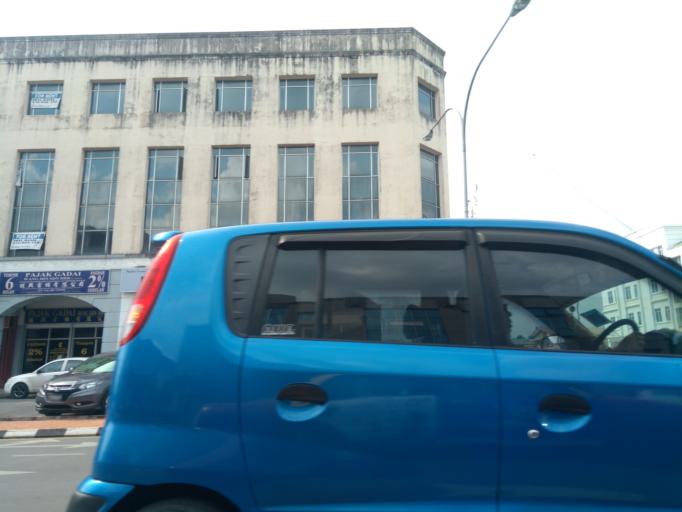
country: MY
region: Sarawak
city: Kuching
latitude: 1.5541
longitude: 110.3359
